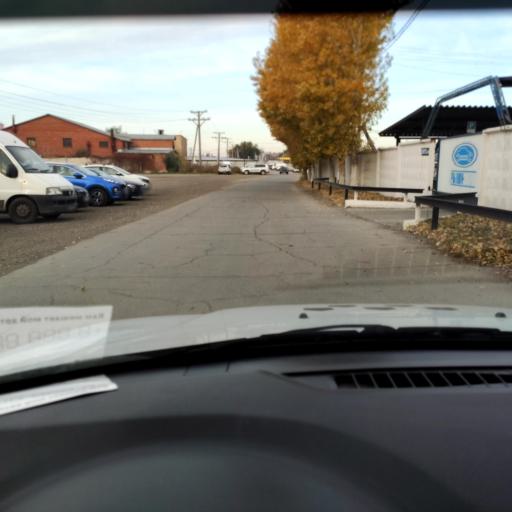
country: RU
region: Samara
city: Tol'yatti
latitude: 53.5697
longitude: 49.4643
